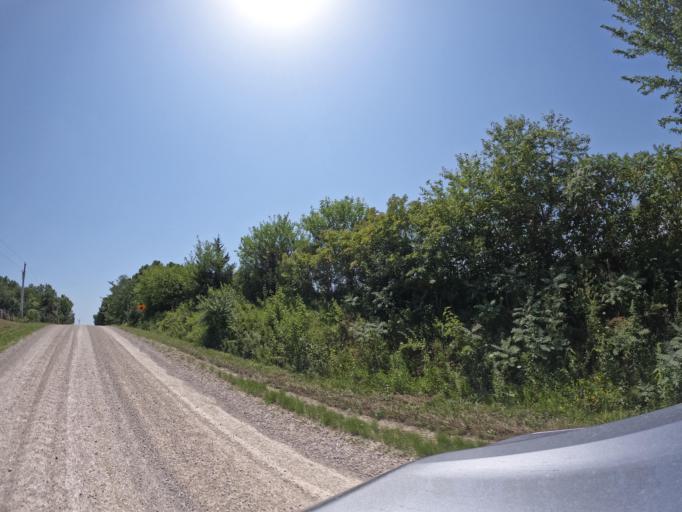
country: US
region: Iowa
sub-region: Henry County
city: Mount Pleasant
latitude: 40.9877
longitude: -91.6363
